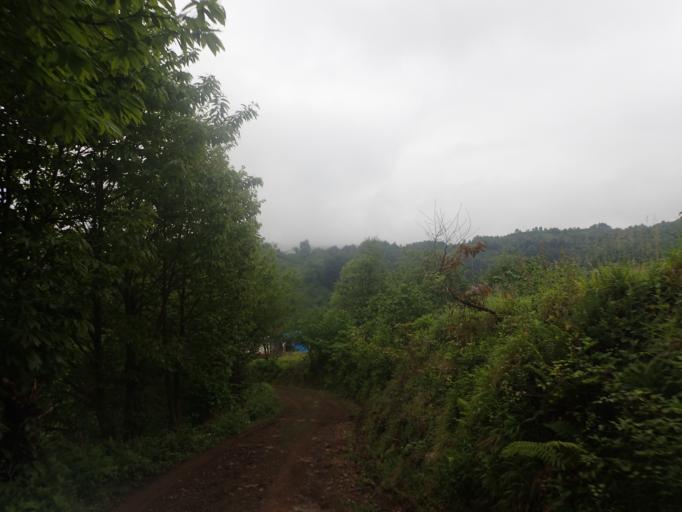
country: TR
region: Samsun
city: Salipazari
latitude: 40.9246
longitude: 36.8872
